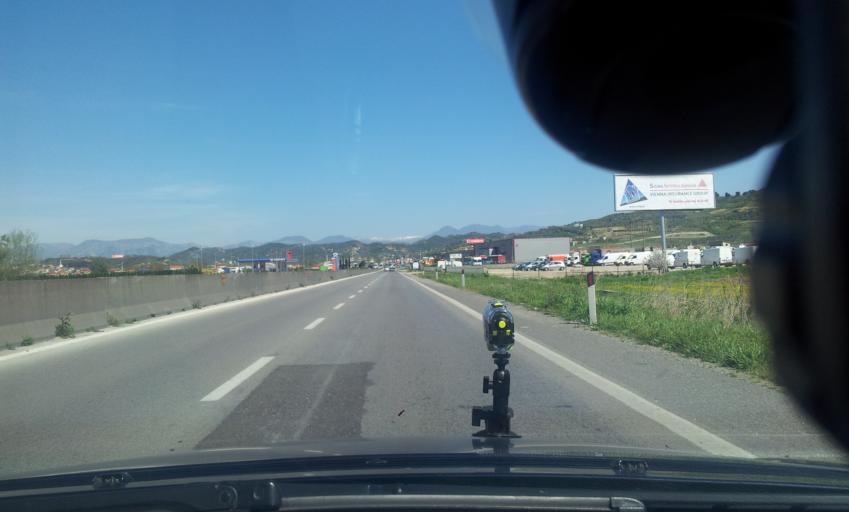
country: AL
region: Durres
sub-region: Rrethi i Durresit
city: Maminas
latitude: 41.3695
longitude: 19.5859
